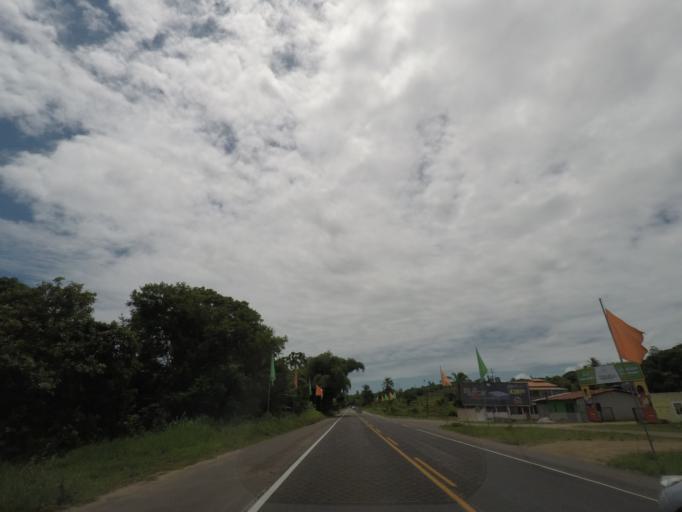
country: BR
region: Bahia
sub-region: Itaparica
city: Itaparica
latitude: -12.9607
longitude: -38.6330
